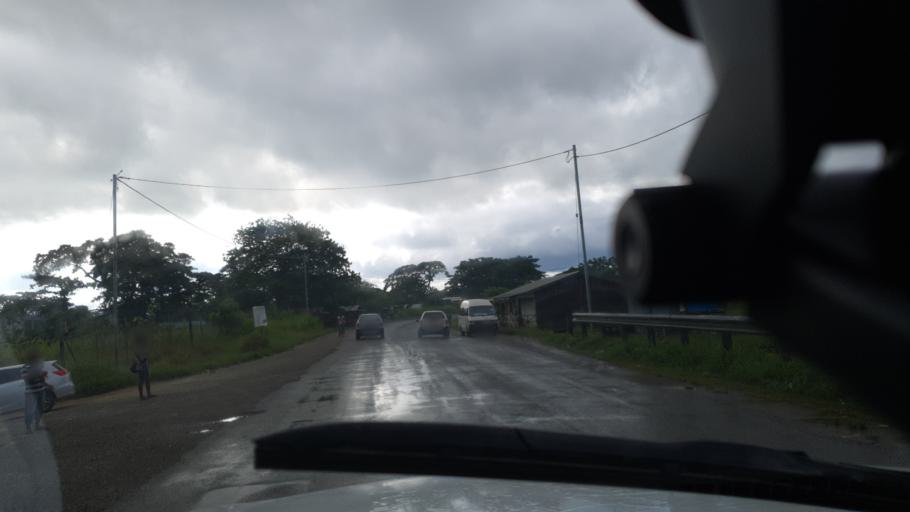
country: SB
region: Guadalcanal
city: Honiara
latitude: -9.4282
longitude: 160.0684
